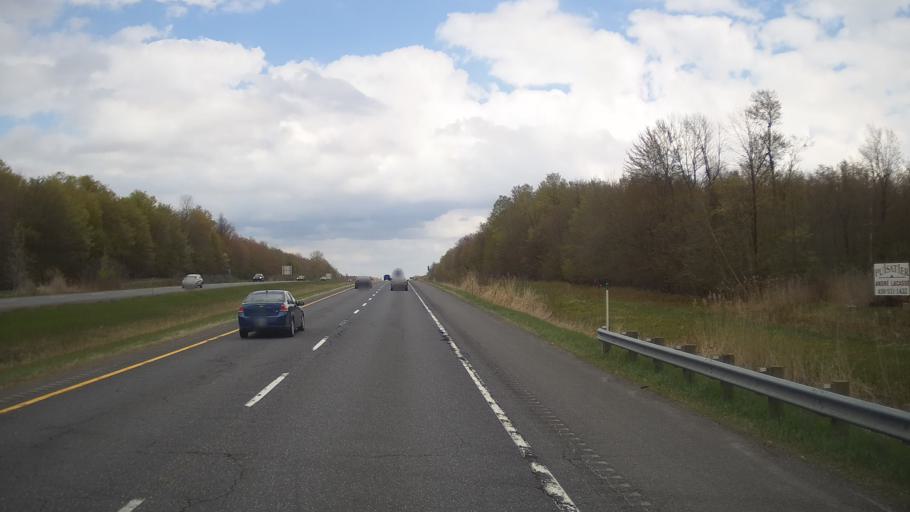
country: CA
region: Quebec
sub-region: Monteregie
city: Saint-Cesaire
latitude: 45.3618
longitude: -72.9223
